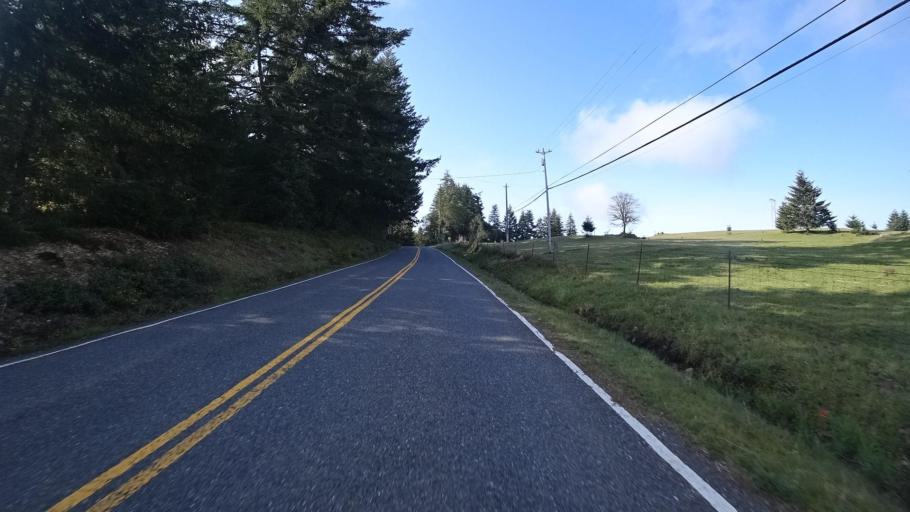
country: US
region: California
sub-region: Humboldt County
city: Blue Lake
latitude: 40.7258
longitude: -123.9449
